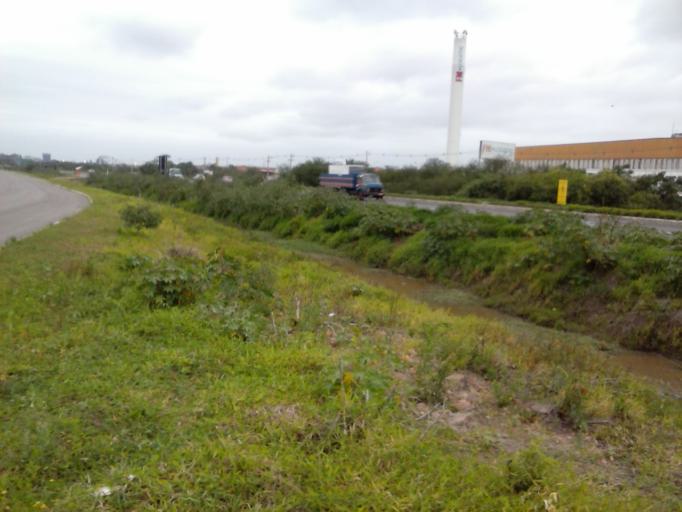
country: BR
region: Rio Grande do Sul
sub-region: Canoas
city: Canoas
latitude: -29.8926
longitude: -51.1921
